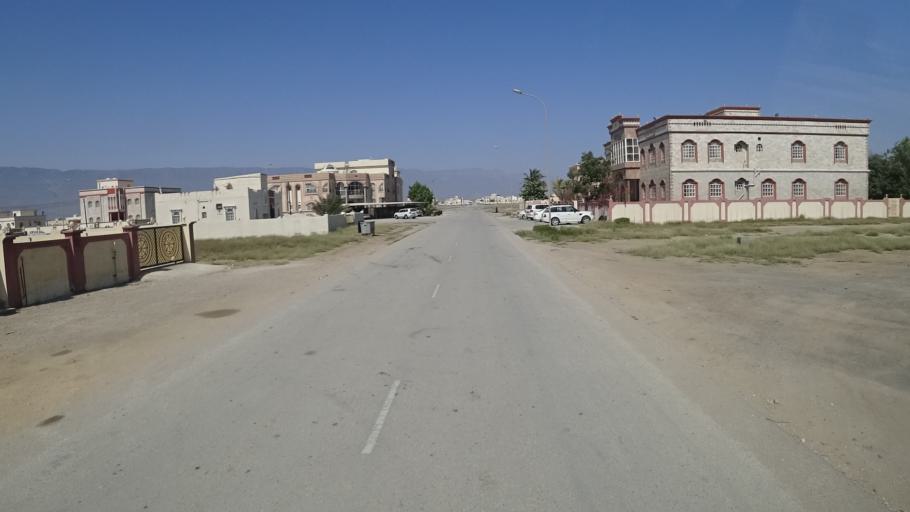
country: OM
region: Zufar
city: Salalah
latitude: 16.9847
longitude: 54.7079
